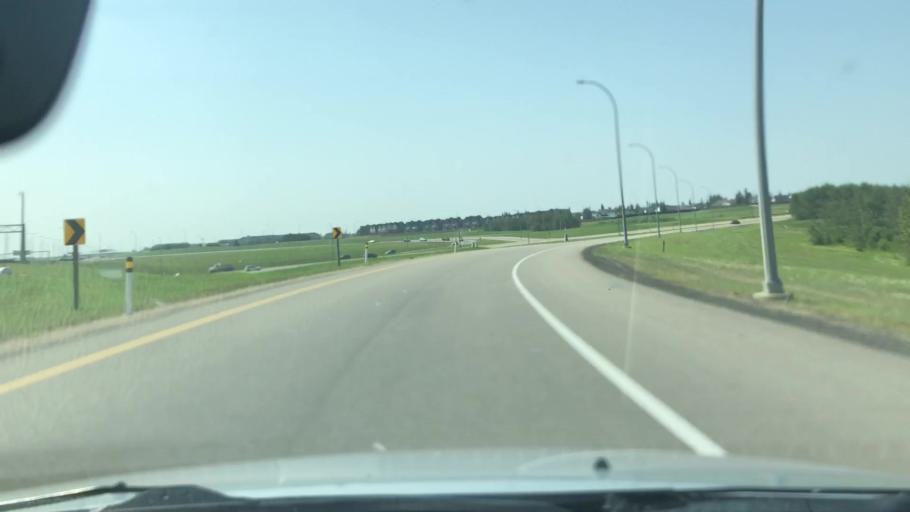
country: CA
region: Alberta
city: St. Albert
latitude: 53.5148
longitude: -113.6600
